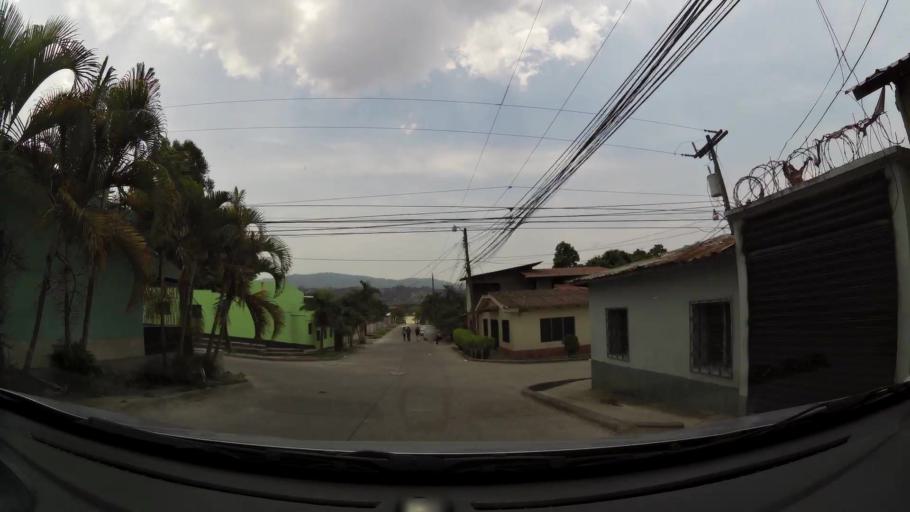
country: HN
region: Comayagua
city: Siguatepeque
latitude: 14.5926
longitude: -87.8303
